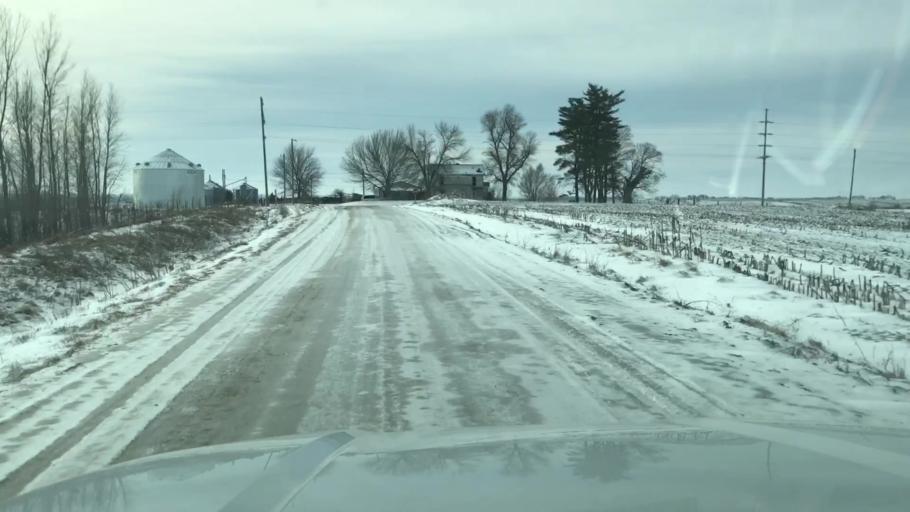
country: US
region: Missouri
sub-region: Holt County
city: Mound City
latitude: 40.1311
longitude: -95.0697
